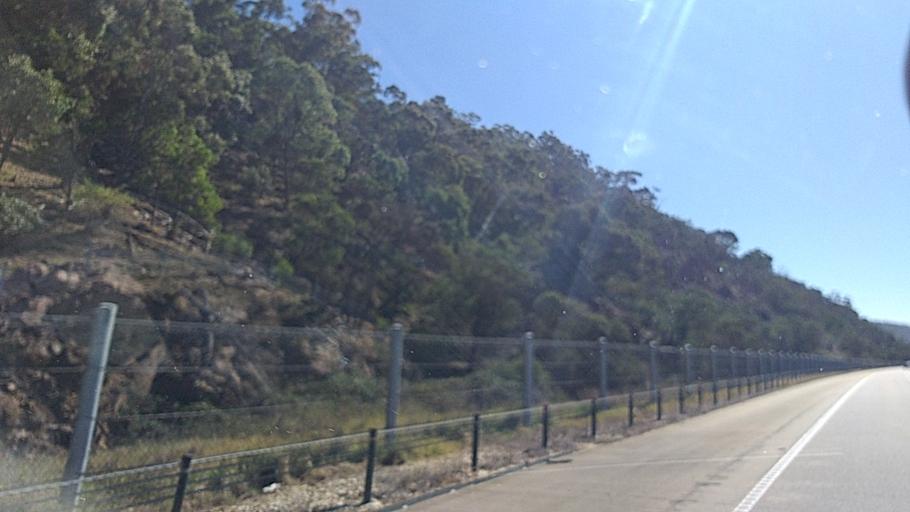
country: AU
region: New South Wales
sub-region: Yass Valley
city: Gundaroo
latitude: -35.0829
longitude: 149.3745
